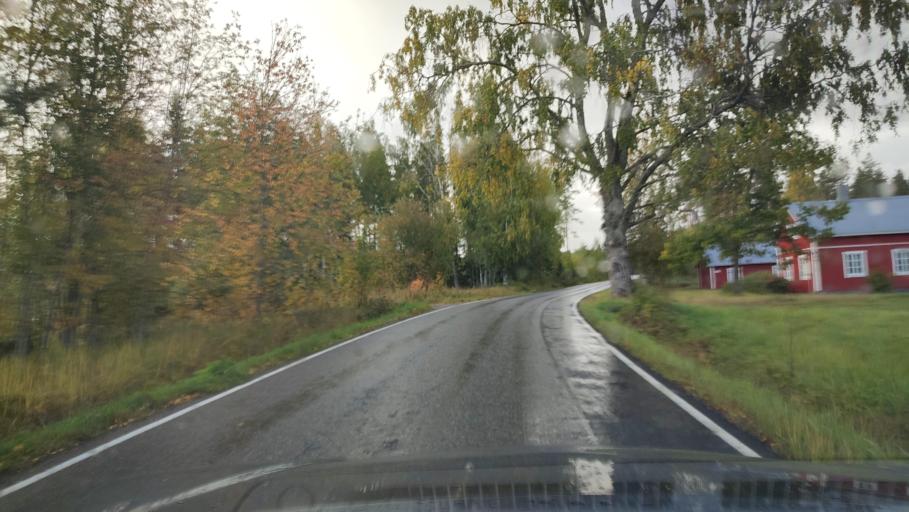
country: FI
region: Southern Ostrobothnia
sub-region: Suupohja
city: Karijoki
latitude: 62.3171
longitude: 21.6845
